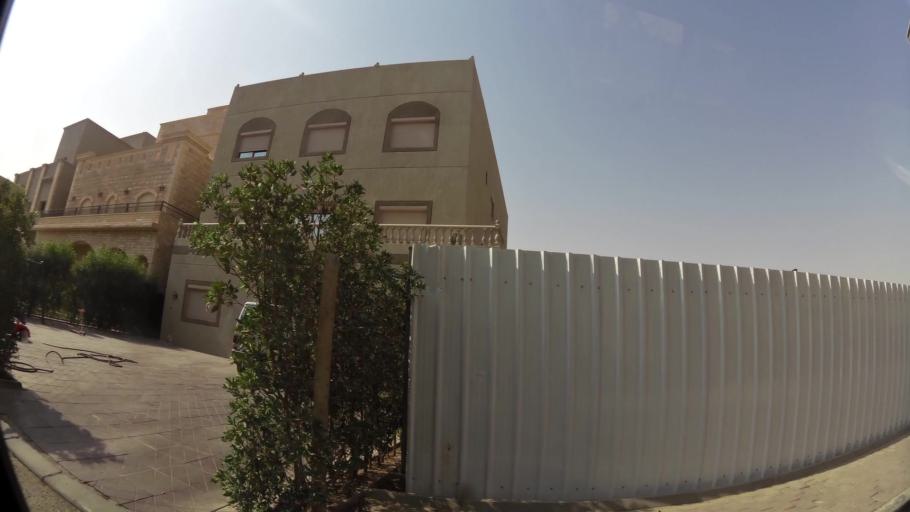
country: KW
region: Muhafazat al Jahra'
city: Al Jahra'
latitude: 29.3389
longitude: 47.7745
